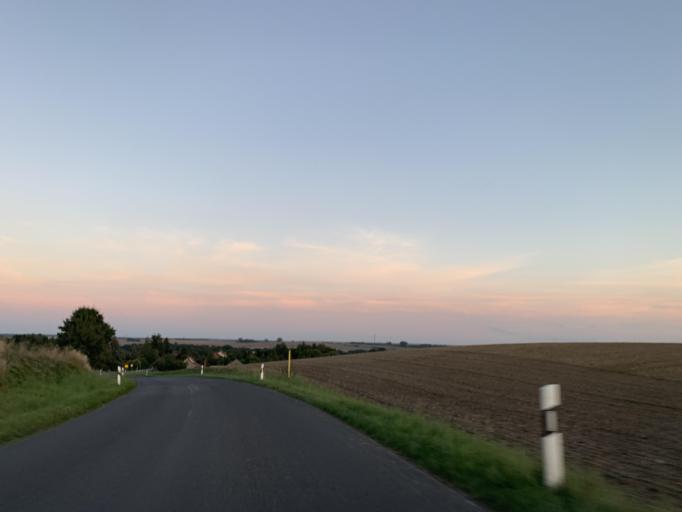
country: DE
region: Mecklenburg-Vorpommern
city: Blankensee
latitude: 53.4456
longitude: 13.2947
